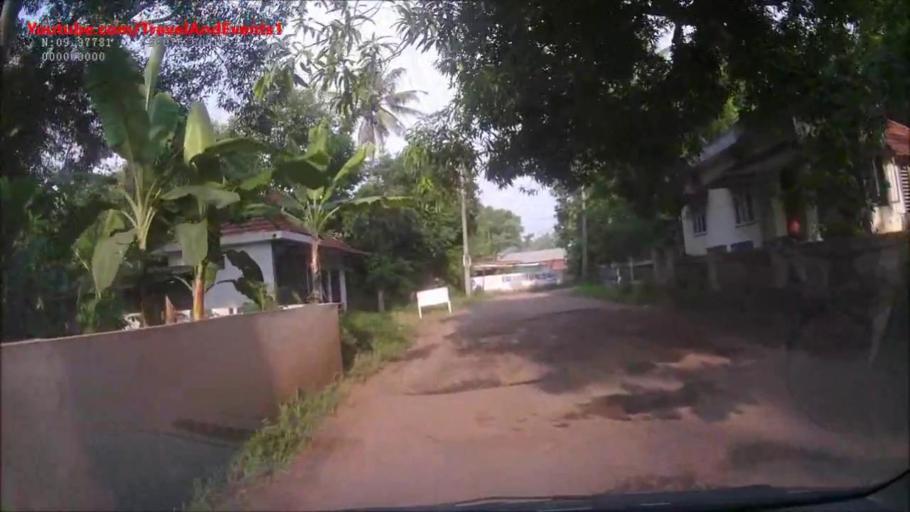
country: IN
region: Kerala
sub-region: Ernakulam
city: Muvattupula
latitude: 9.9730
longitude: 76.6048
